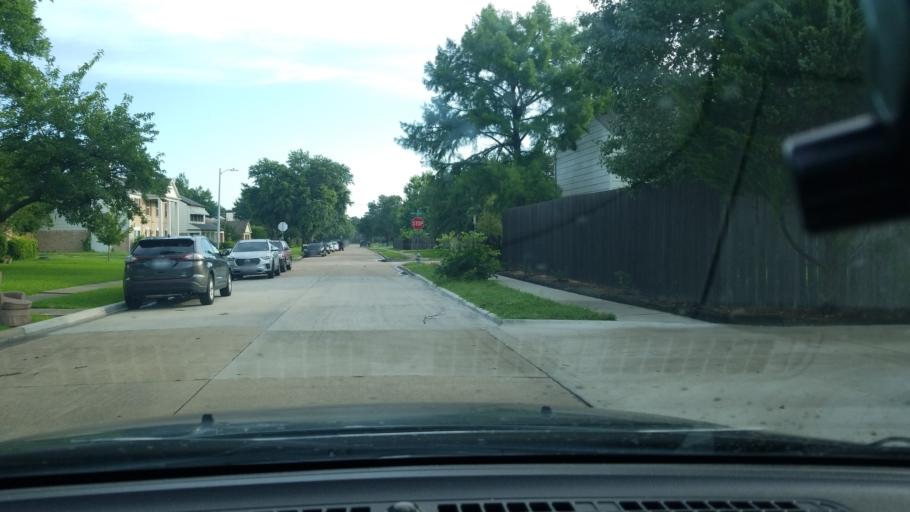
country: US
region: Texas
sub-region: Dallas County
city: Mesquite
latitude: 32.7949
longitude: -96.6019
